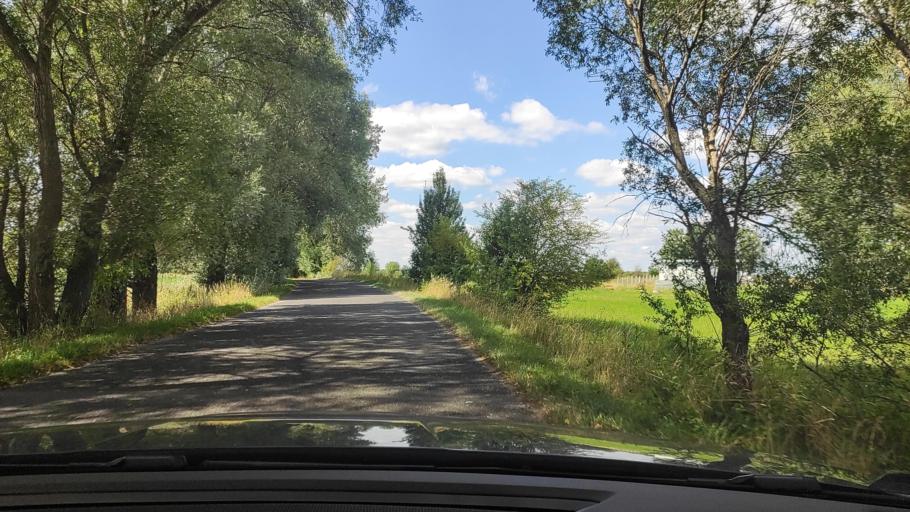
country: PL
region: Greater Poland Voivodeship
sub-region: Powiat poznanski
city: Kobylnica
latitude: 52.4949
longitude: 17.1291
